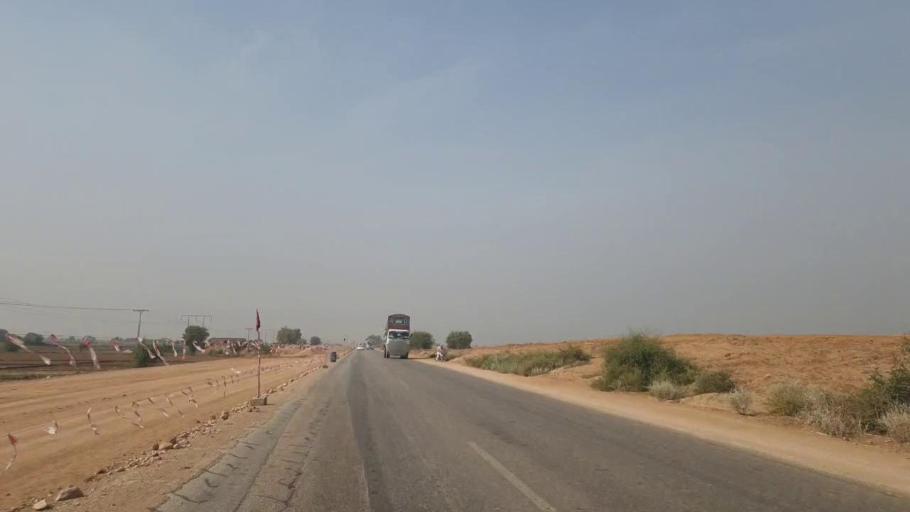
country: PK
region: Sindh
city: Sann
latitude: 26.1308
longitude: 68.0490
